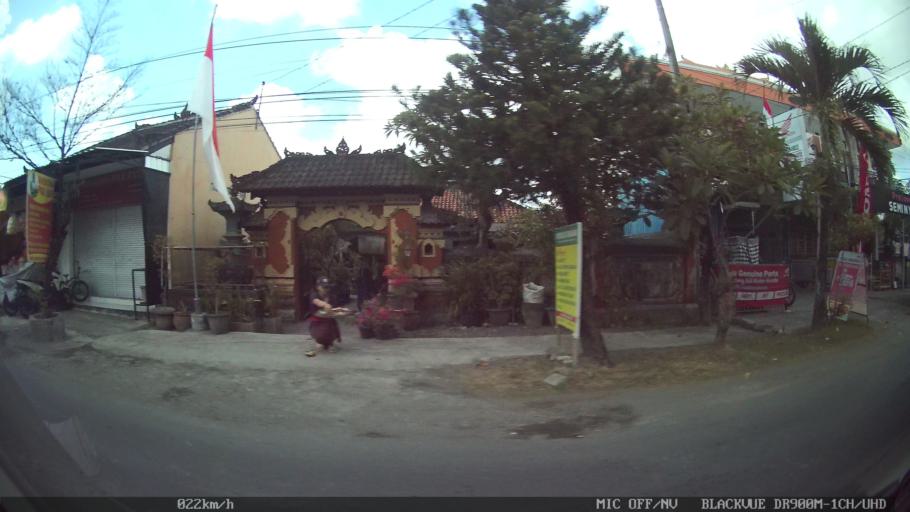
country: ID
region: Bali
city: Jabajero
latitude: -8.7205
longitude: 115.1898
